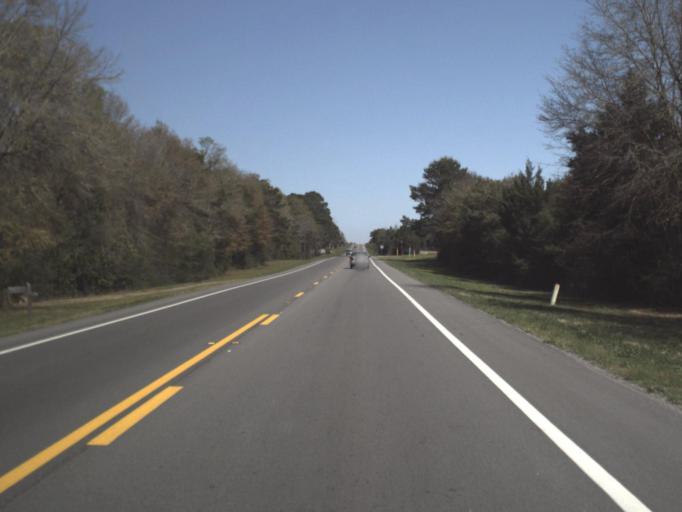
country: US
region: Florida
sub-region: Walton County
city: DeFuniak Springs
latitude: 30.7406
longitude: -86.1848
